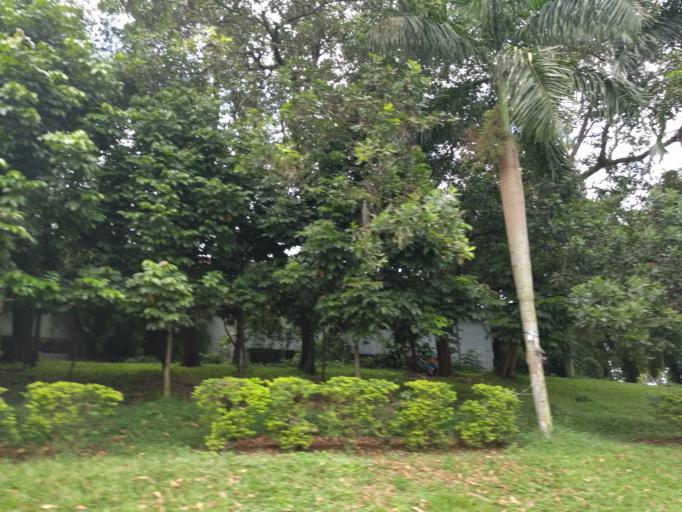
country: ID
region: West Java
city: Bogor
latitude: -6.6043
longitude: 106.8076
